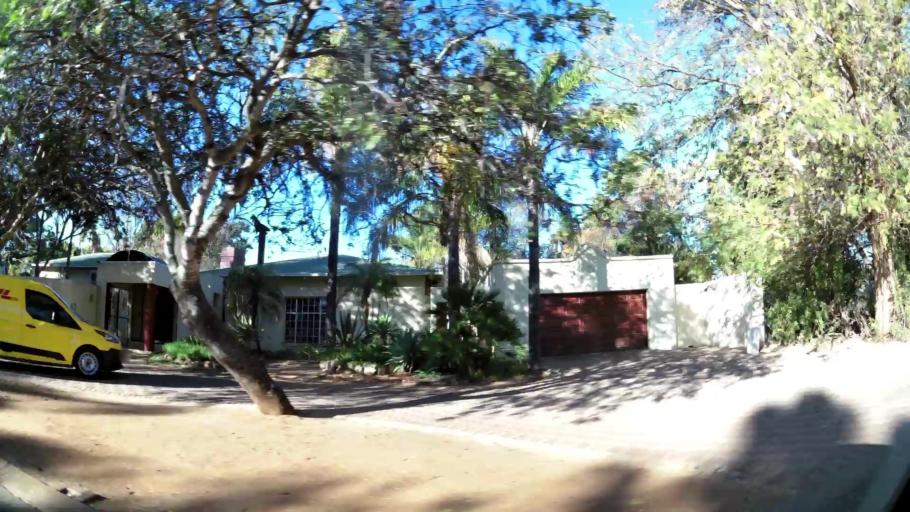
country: ZA
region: Limpopo
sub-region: Capricorn District Municipality
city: Polokwane
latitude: -23.9097
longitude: 29.4689
